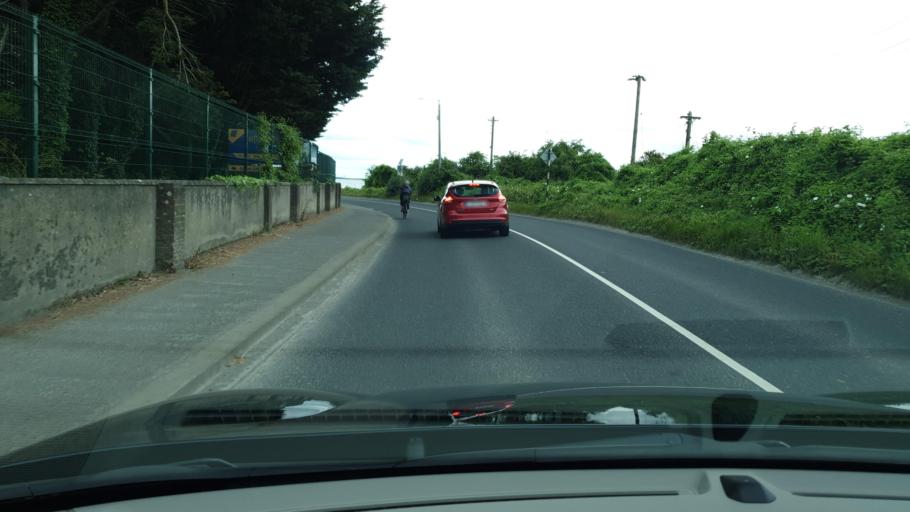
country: IE
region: Leinster
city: Kinsealy-Drinan
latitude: 53.4375
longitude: -6.1870
